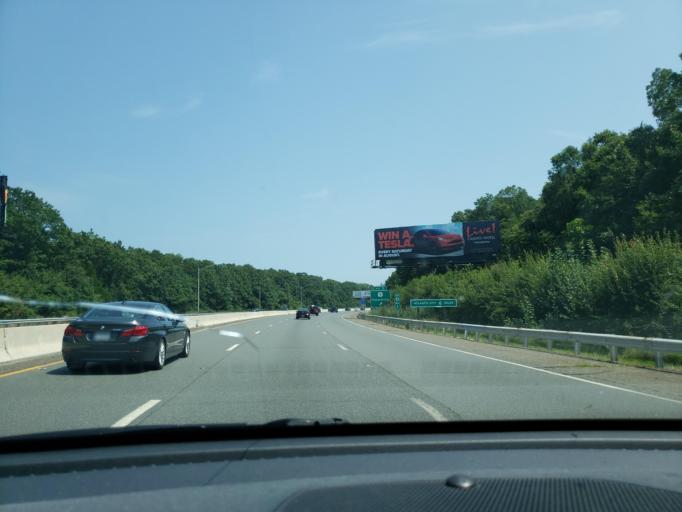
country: US
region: New Jersey
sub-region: Atlantic County
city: Pleasantville
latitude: 39.4057
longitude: -74.5343
